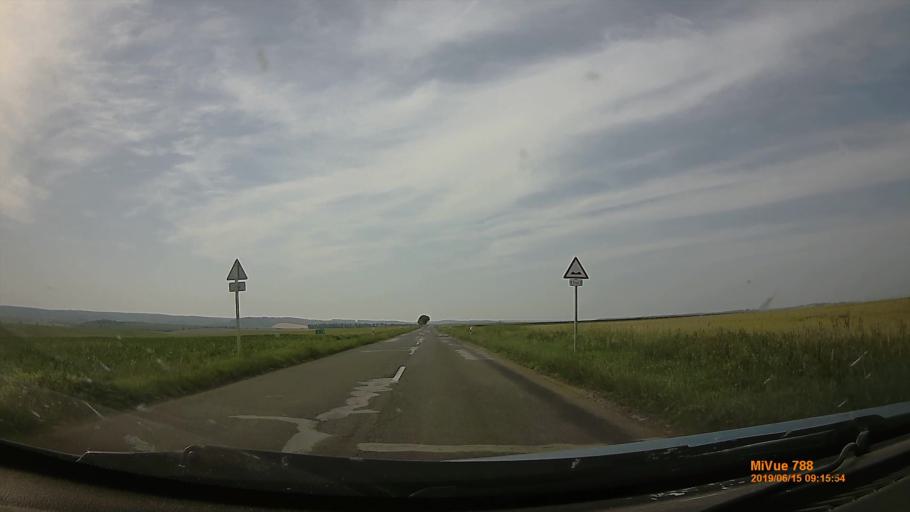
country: HU
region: Tolna
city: Iregszemcse
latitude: 46.6232
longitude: 18.2027
